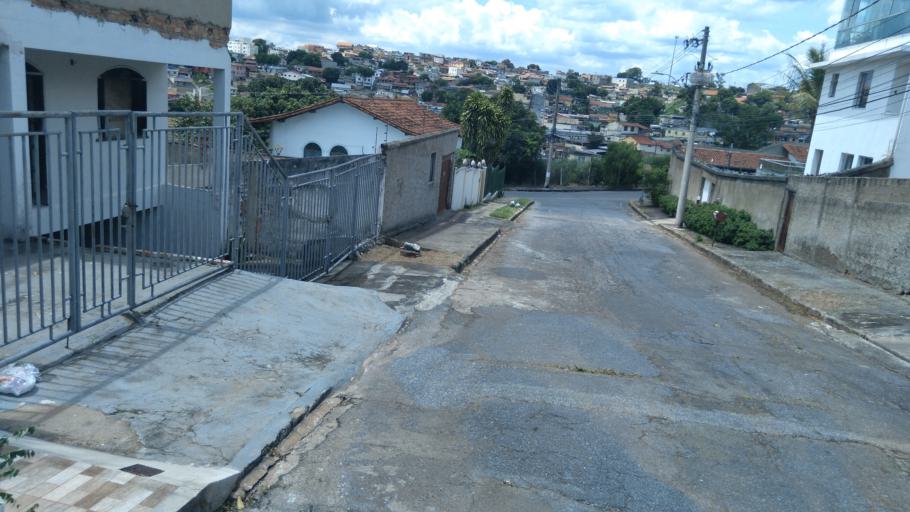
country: BR
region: Minas Gerais
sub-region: Contagem
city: Contagem
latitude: -19.9166
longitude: -44.0068
